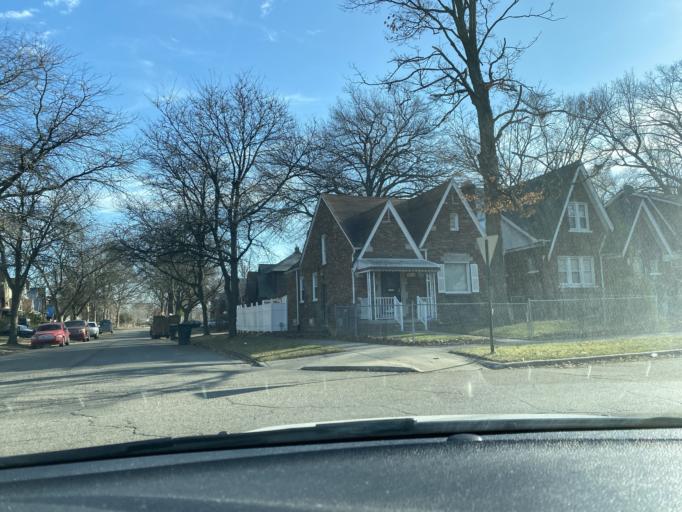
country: US
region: Michigan
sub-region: Wayne County
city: Harper Woods
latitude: 42.4109
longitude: -82.9504
